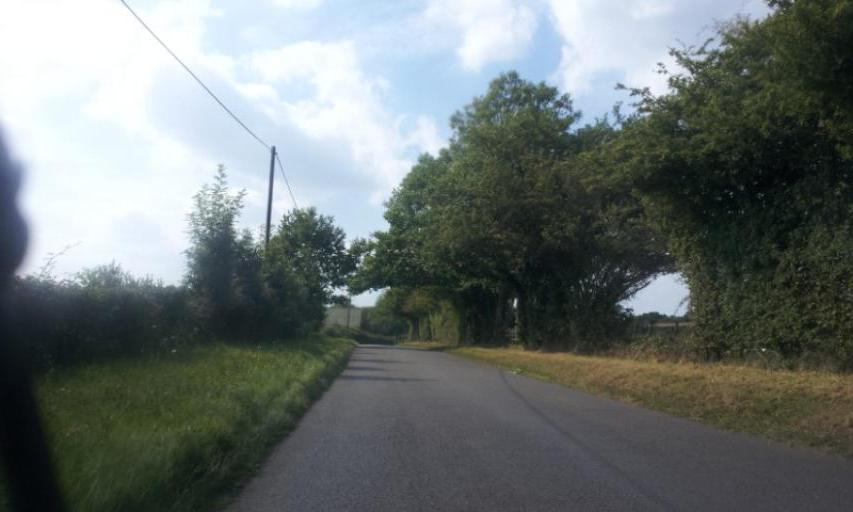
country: GB
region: England
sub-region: Kent
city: Marden
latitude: 51.2149
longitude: 0.4877
